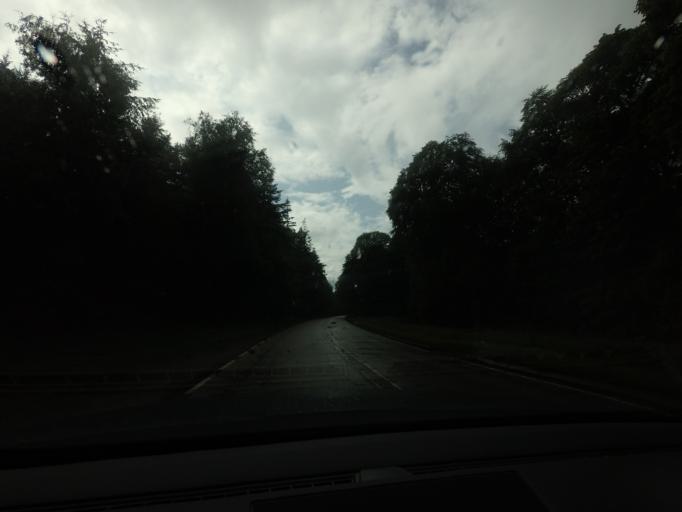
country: GB
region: Scotland
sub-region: Moray
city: Fochabers
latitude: 57.6158
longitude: -3.0672
